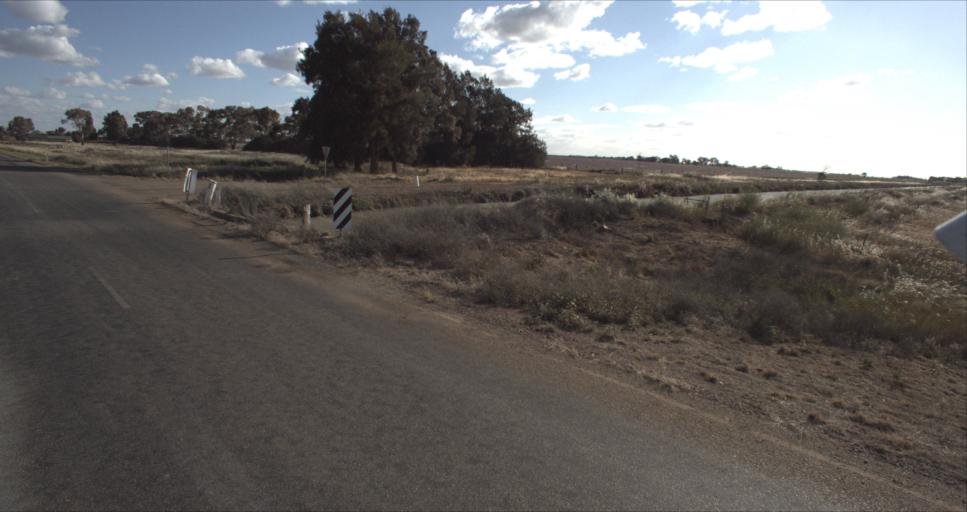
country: AU
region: New South Wales
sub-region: Leeton
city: Leeton
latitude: -34.5375
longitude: 146.2803
